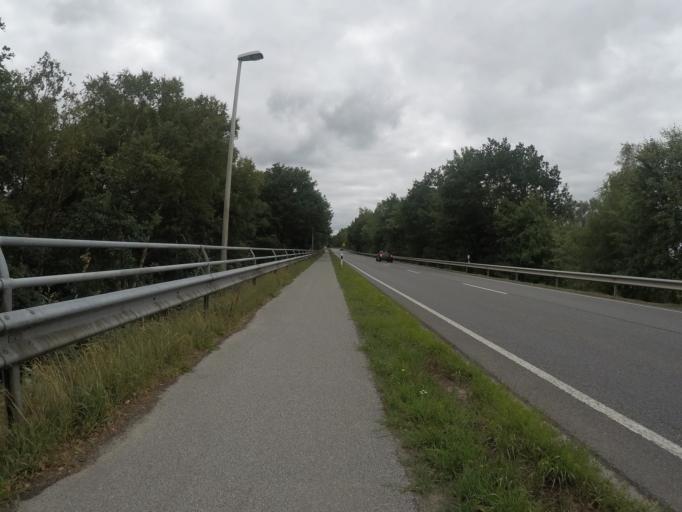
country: DE
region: Lower Saxony
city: Hemmoor
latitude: 53.6923
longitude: 9.1738
